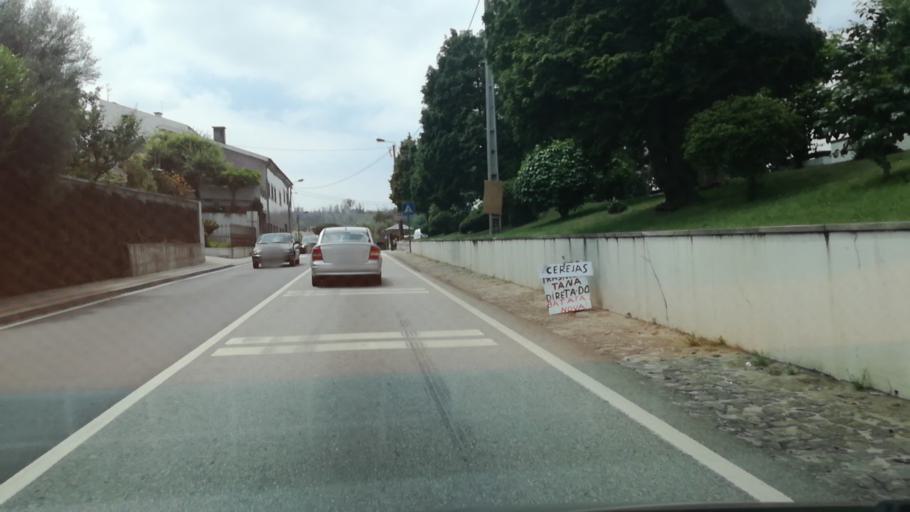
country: PT
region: Porto
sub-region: Trofa
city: Bougado
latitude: 41.3193
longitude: -8.5744
